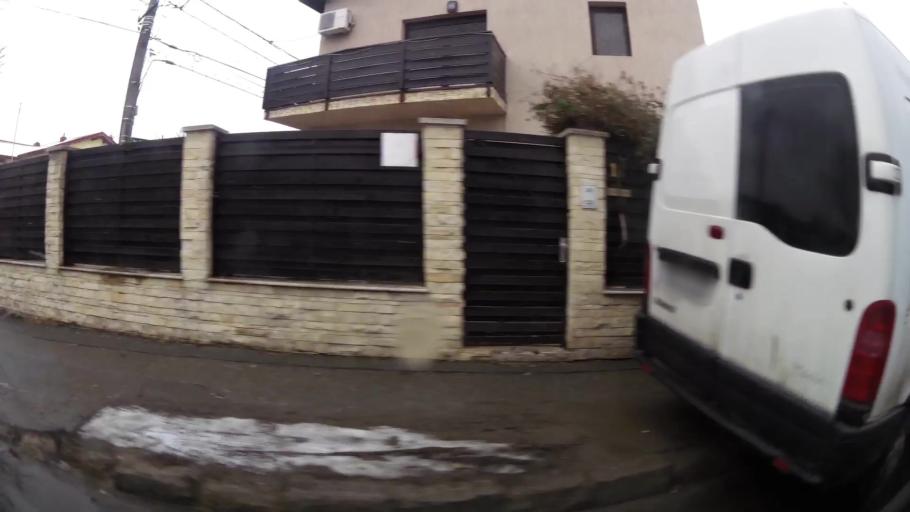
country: RO
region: Ilfov
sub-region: Comuna Mogosoaia
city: Mogosoaia
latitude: 44.4958
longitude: 26.0277
